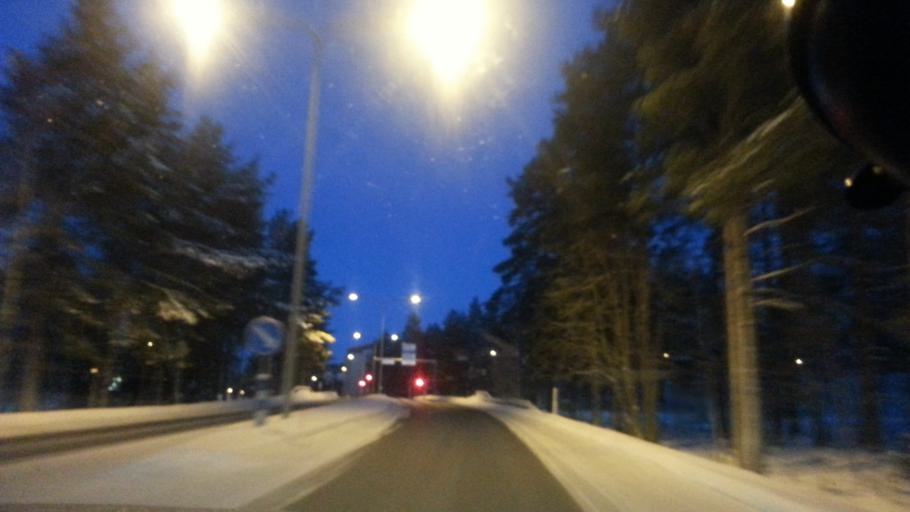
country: FI
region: Lapland
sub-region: Rovaniemi
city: Rovaniemi
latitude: 66.4961
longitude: 25.7569
